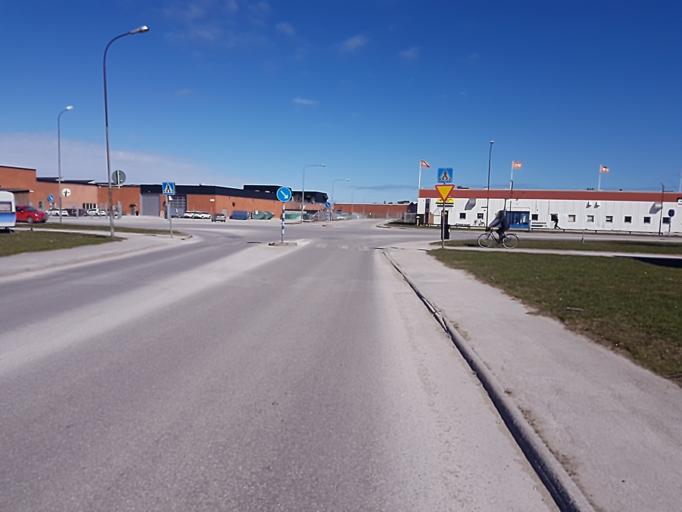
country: SE
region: Gotland
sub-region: Gotland
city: Visby
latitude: 57.6420
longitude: 18.3164
